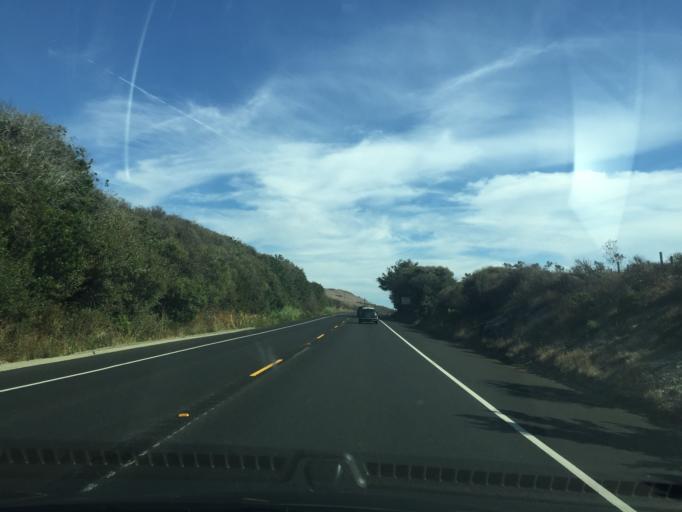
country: US
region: California
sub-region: Santa Cruz County
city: Bonny Doon
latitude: 36.9799
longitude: -122.1380
